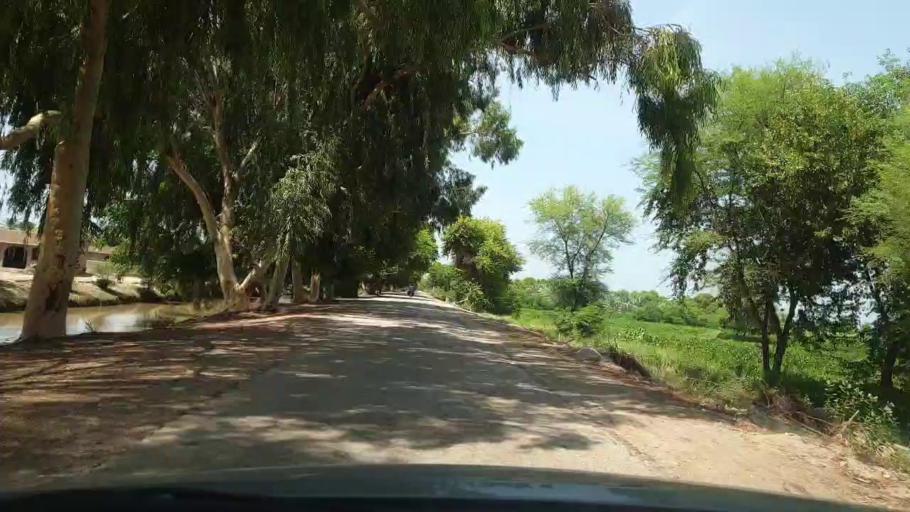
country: PK
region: Sindh
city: Pano Aqil
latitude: 27.6976
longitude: 69.1115
